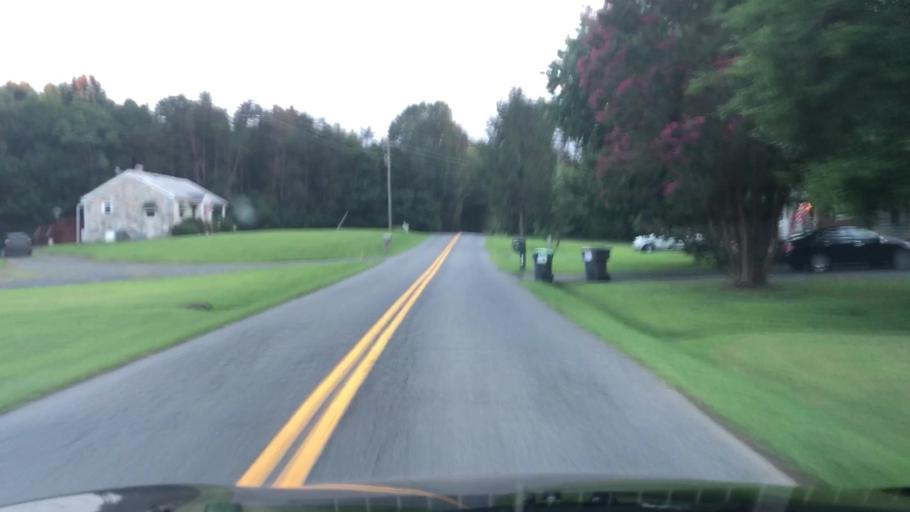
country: US
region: Virginia
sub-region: Stafford County
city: Stafford
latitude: 38.4830
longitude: -77.5788
